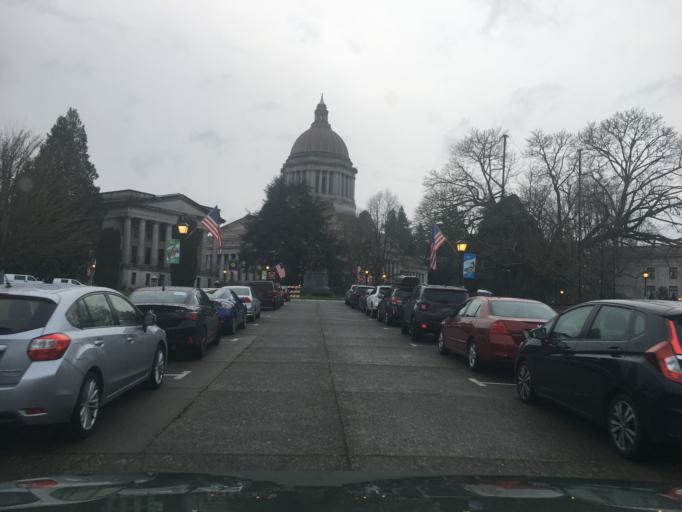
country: US
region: Washington
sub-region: Thurston County
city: Olympia
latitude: 47.0370
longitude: -122.9023
